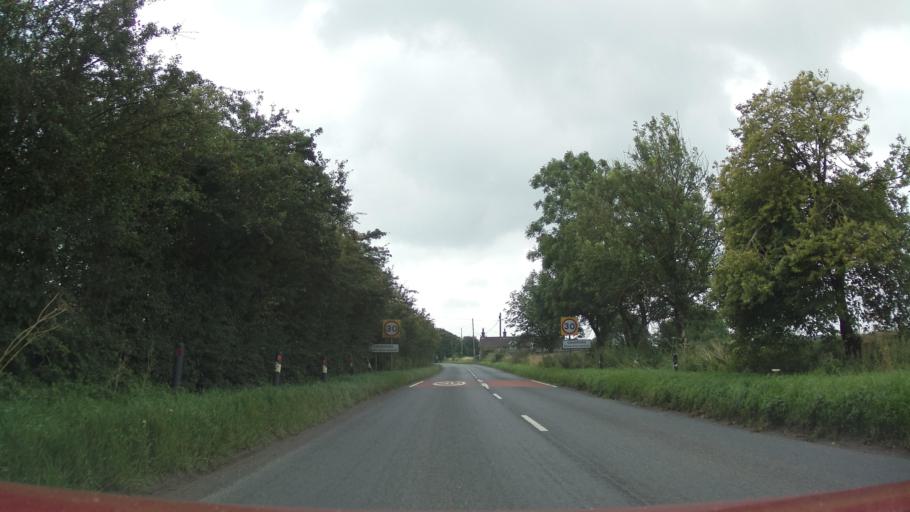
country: GB
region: England
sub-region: Somerset
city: Evercreech
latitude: 51.1923
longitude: -2.4841
